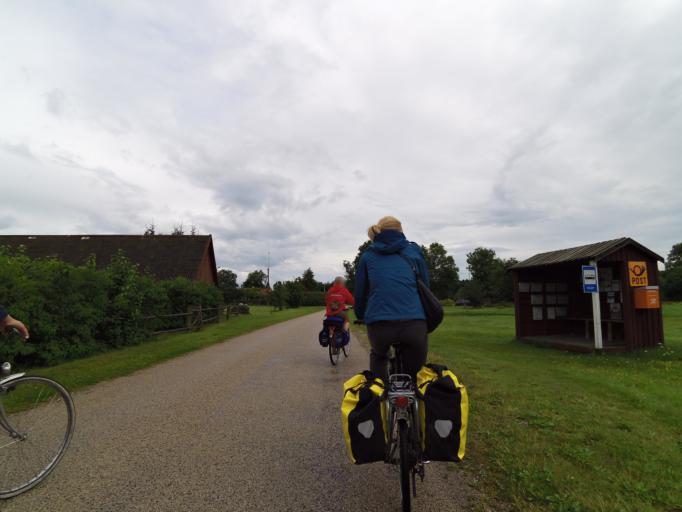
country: EE
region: Laeaene
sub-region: Vormsi vald
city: Hullo
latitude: 59.0126
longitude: 23.2846
